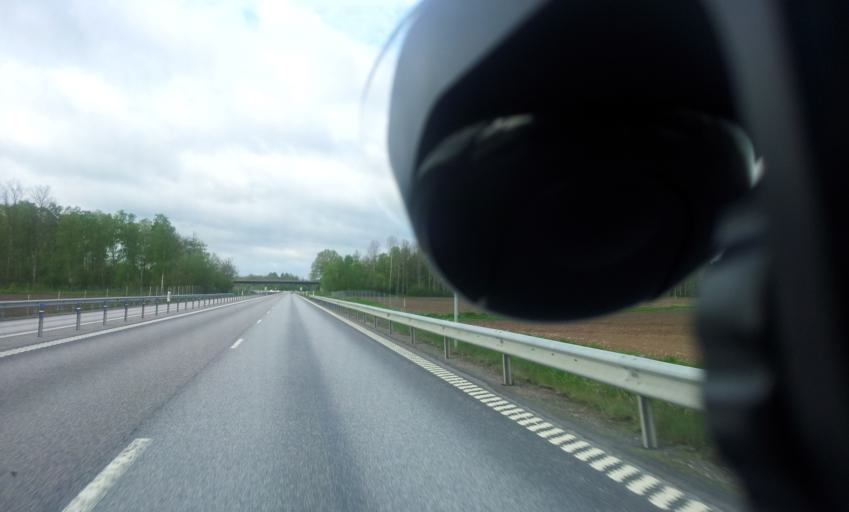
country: SE
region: Kalmar
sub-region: Kalmar Kommun
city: Ljungbyholm
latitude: 56.5730
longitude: 16.1022
